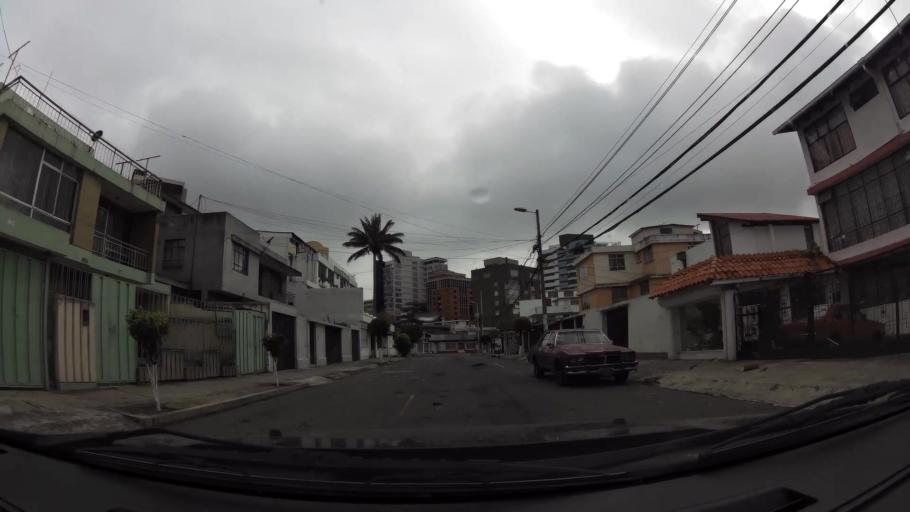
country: EC
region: Pichincha
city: Quito
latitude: -0.1874
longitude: -78.4890
